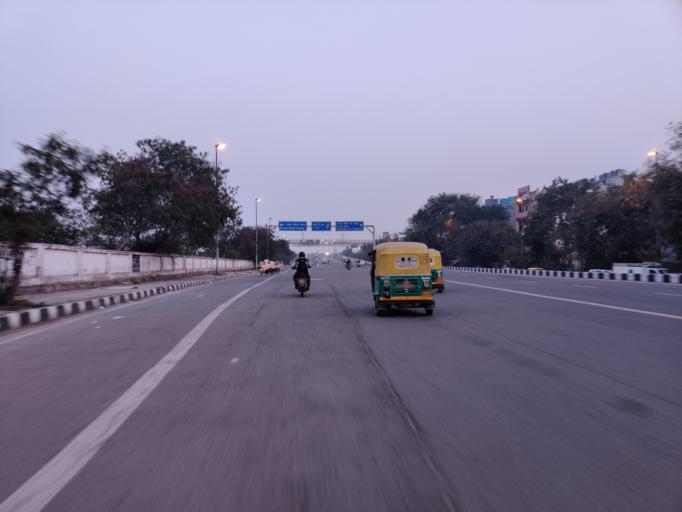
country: IN
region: NCT
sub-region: North Delhi
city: Delhi
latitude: 28.6472
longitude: 77.2962
